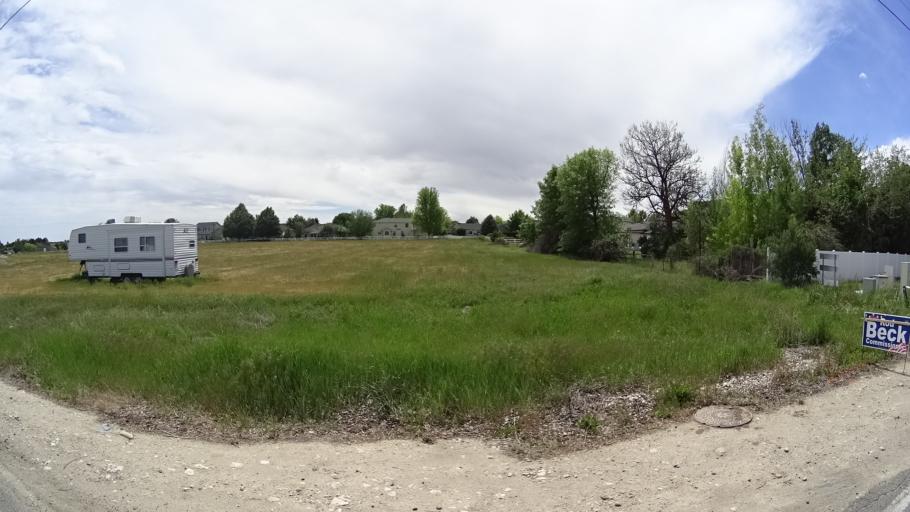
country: US
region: Idaho
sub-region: Ada County
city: Meridian
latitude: 43.5756
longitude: -116.4035
